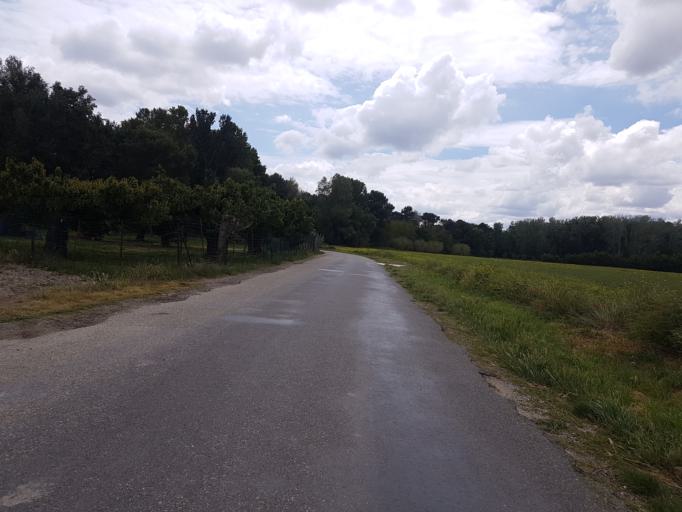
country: FR
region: Languedoc-Roussillon
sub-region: Departement du Gard
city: Vallabregues
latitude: 43.8669
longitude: 4.6191
